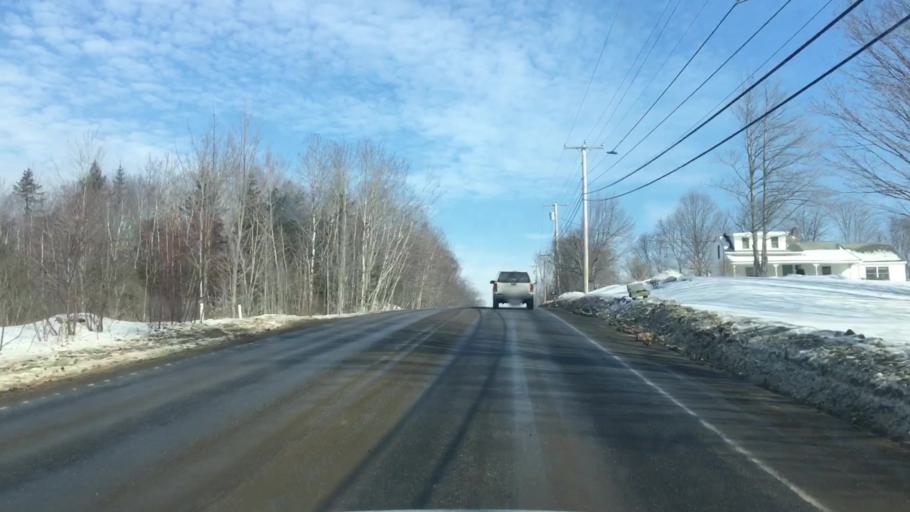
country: US
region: Maine
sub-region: Penobscot County
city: Hermon
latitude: 44.8327
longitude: -68.8799
